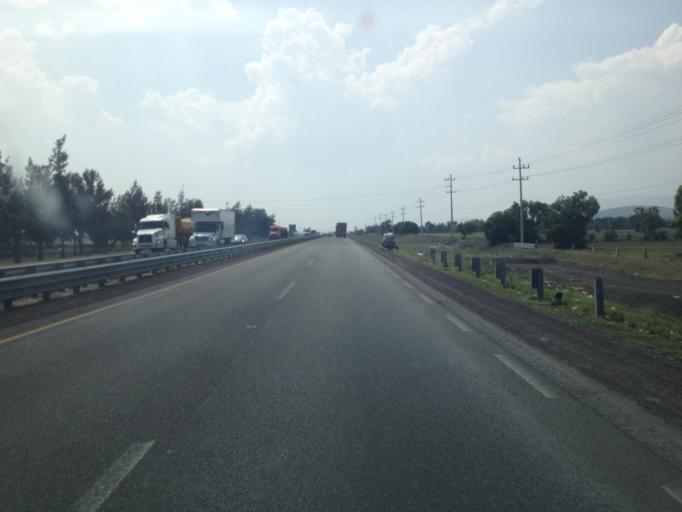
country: MX
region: Puebla
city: Cuacnopalan
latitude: 18.8344
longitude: -97.5126
